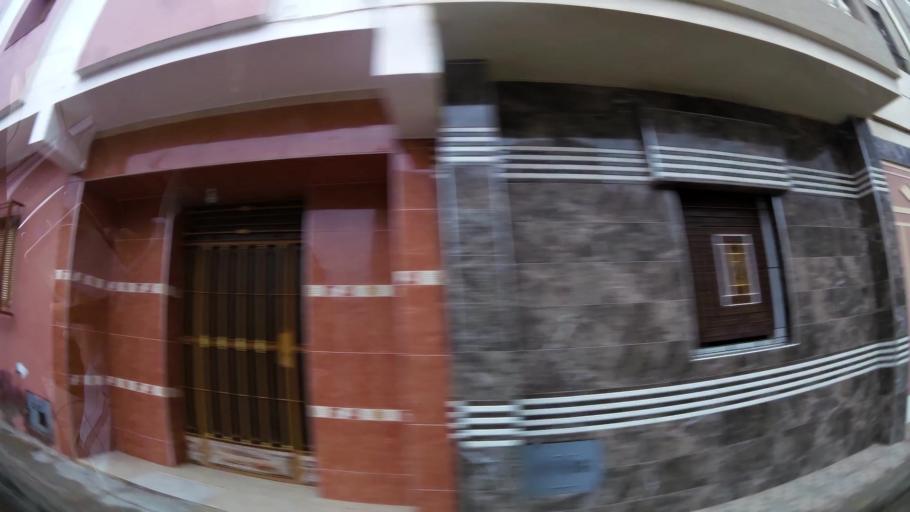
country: MA
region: Oriental
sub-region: Nador
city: Nador
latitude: 35.1577
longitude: -2.9524
